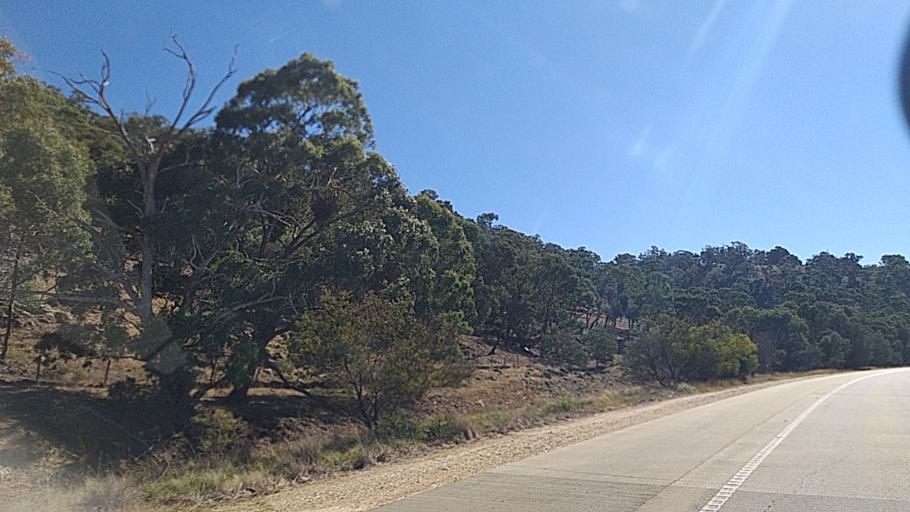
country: AU
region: New South Wales
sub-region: Yass Valley
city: Gundaroo
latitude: -35.0899
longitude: 149.3749
